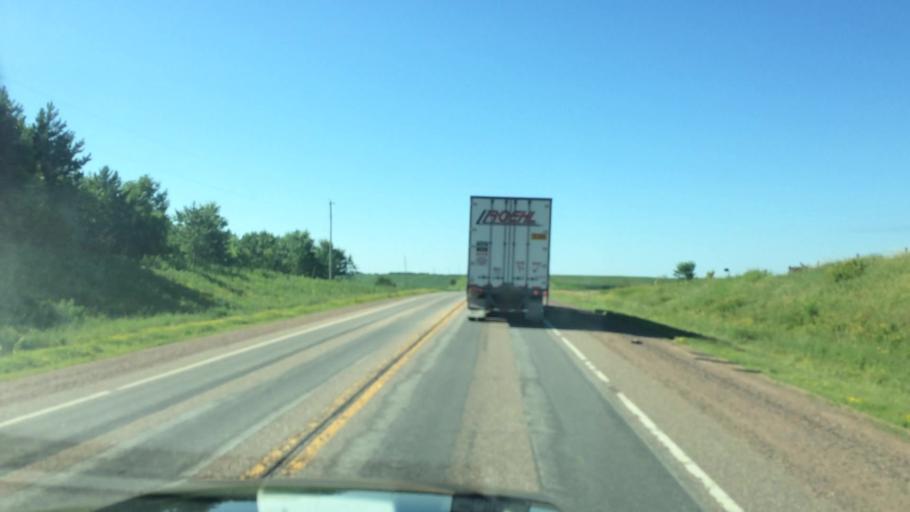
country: US
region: Wisconsin
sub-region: Marathon County
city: Athens
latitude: 44.9253
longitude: -90.0788
